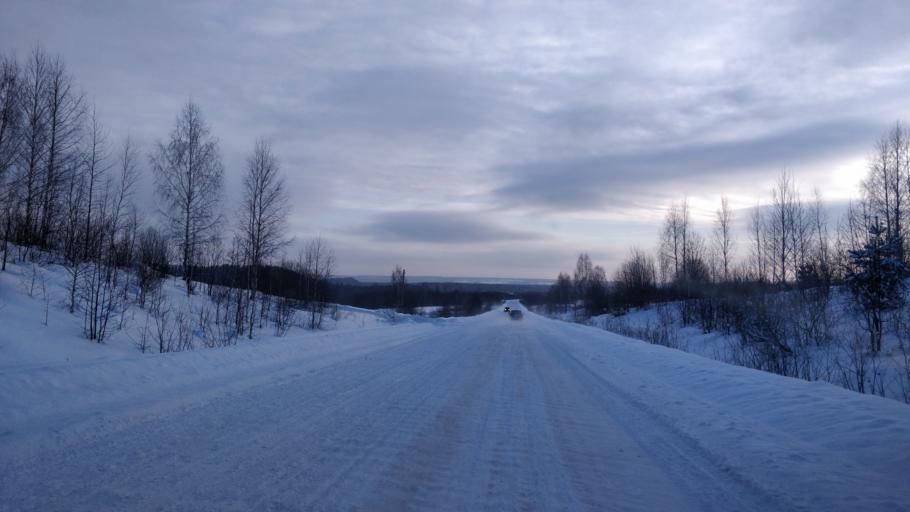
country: RU
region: Perm
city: Verkhnechusovskiye Gorodki
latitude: 58.2098
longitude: 57.1424
